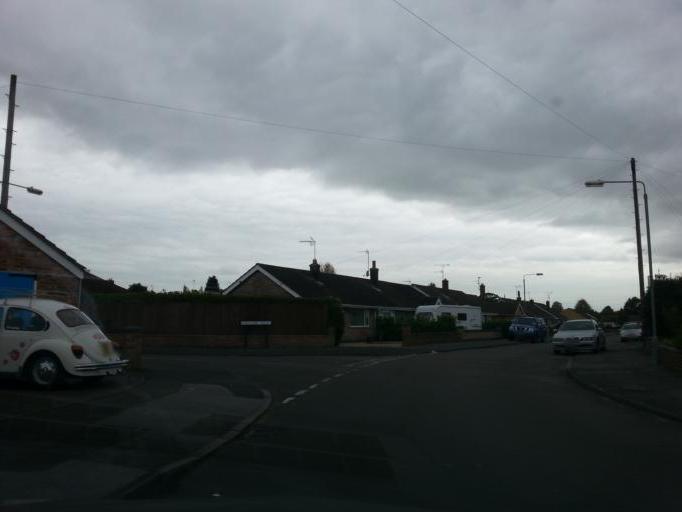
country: GB
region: England
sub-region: Nottinghamshire
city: Newark on Trent
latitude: 53.0592
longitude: -0.7775
